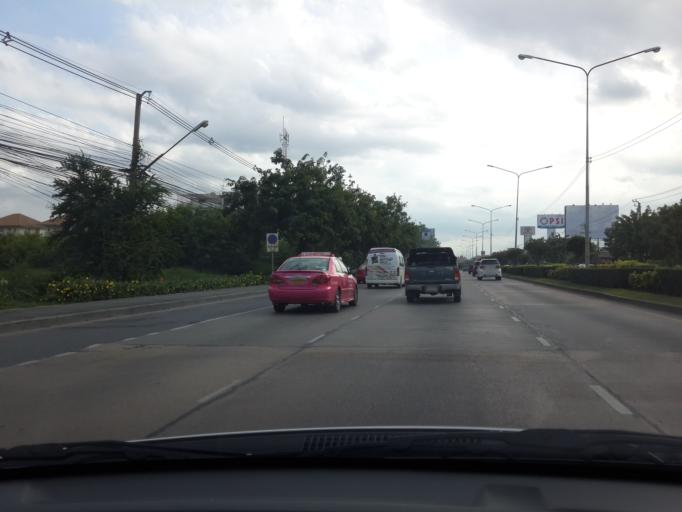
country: TH
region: Bangkok
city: Saphan Sung
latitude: 13.7919
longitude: 100.7008
